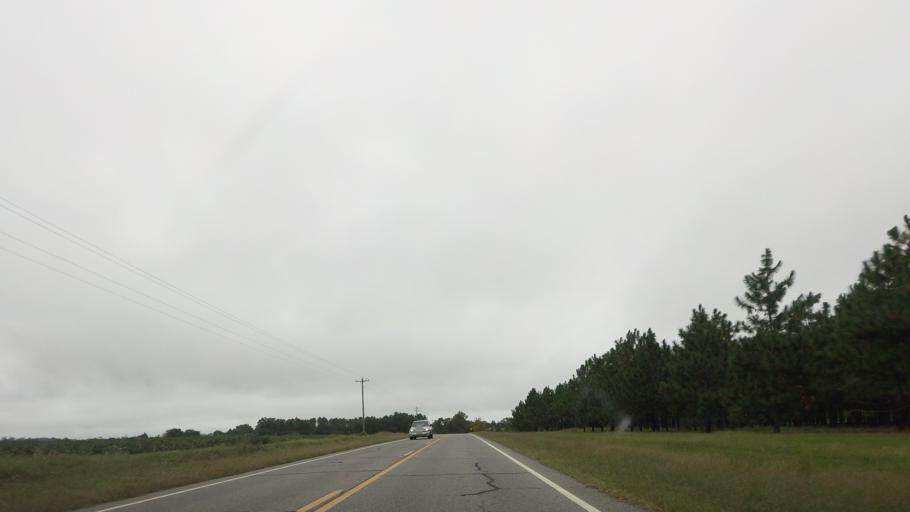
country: US
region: Georgia
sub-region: Irwin County
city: Ocilla
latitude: 31.5072
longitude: -83.2390
